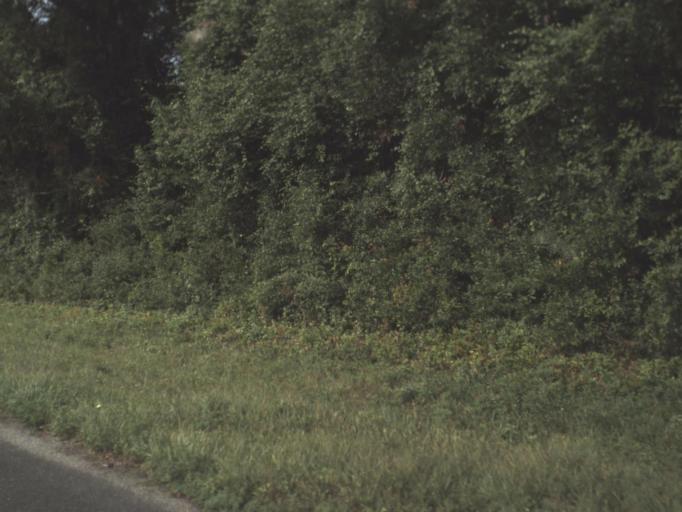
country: US
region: Florida
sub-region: Taylor County
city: Perry
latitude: 30.2966
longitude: -83.6349
